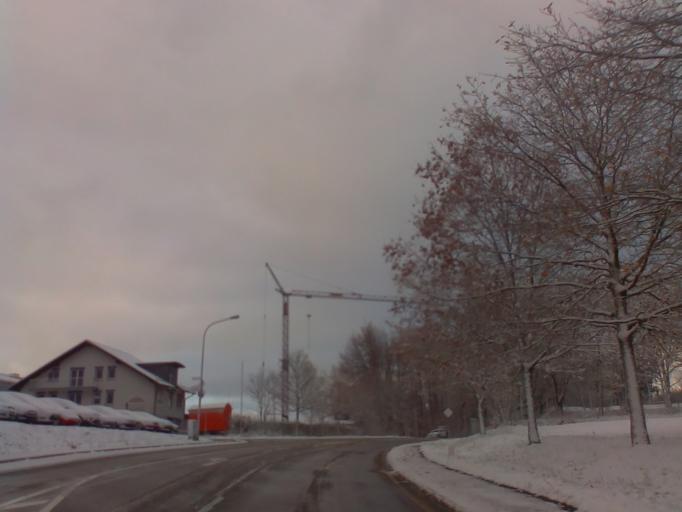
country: DE
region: Hesse
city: Unter-Abtsteinach
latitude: 49.5440
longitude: 8.7946
